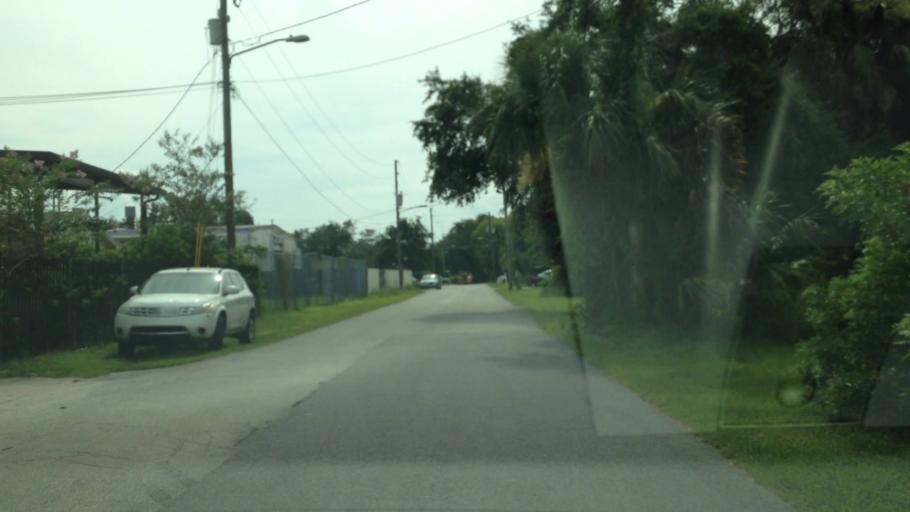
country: US
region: Florida
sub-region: Seminole County
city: Fern Park
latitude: 28.6642
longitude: -81.3474
